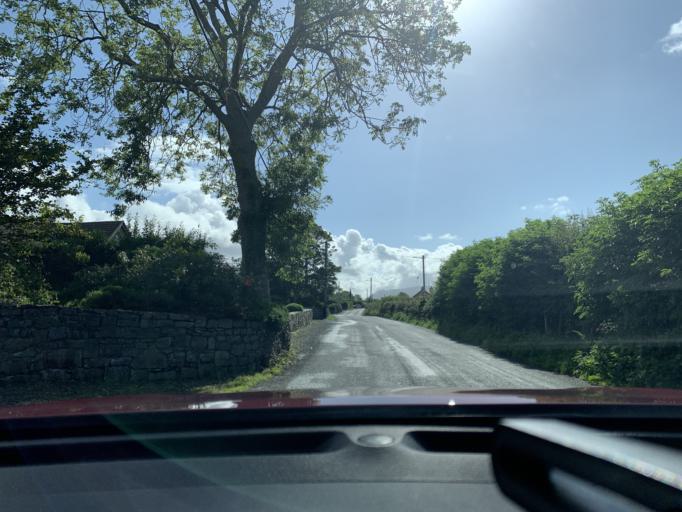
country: IE
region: Connaught
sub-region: Sligo
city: Strandhill
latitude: 54.3387
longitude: -8.5354
